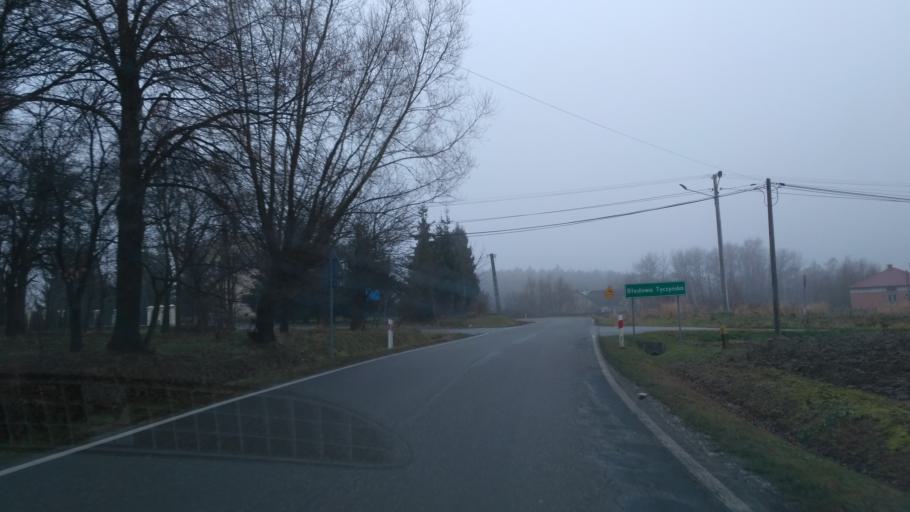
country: PL
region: Subcarpathian Voivodeship
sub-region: Powiat lancucki
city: Handzlowka
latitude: 49.9753
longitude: 22.1906
